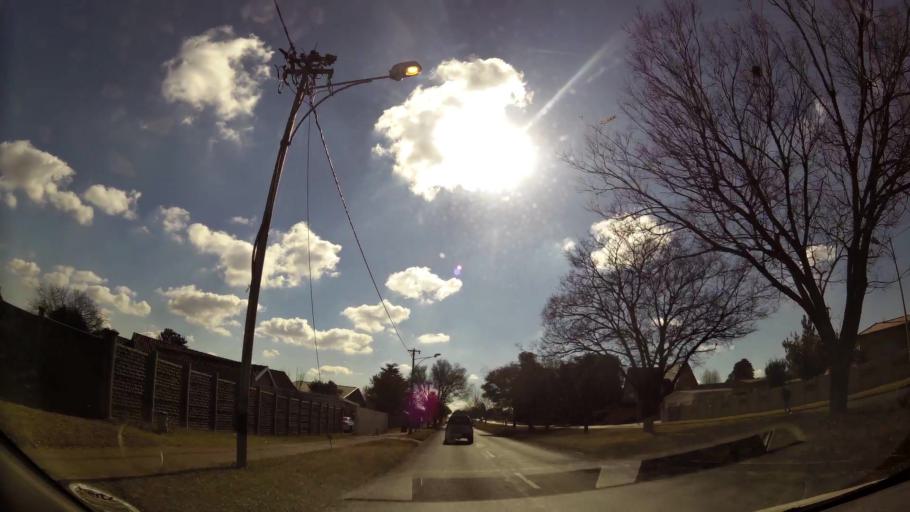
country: ZA
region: Gauteng
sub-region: City of Johannesburg Metropolitan Municipality
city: Roodepoort
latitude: -26.1338
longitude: 27.8313
